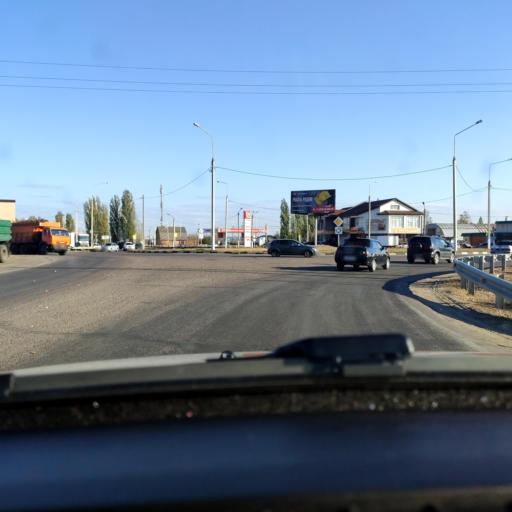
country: RU
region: Voronezj
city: Semiluki
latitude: 51.7261
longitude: 39.0344
